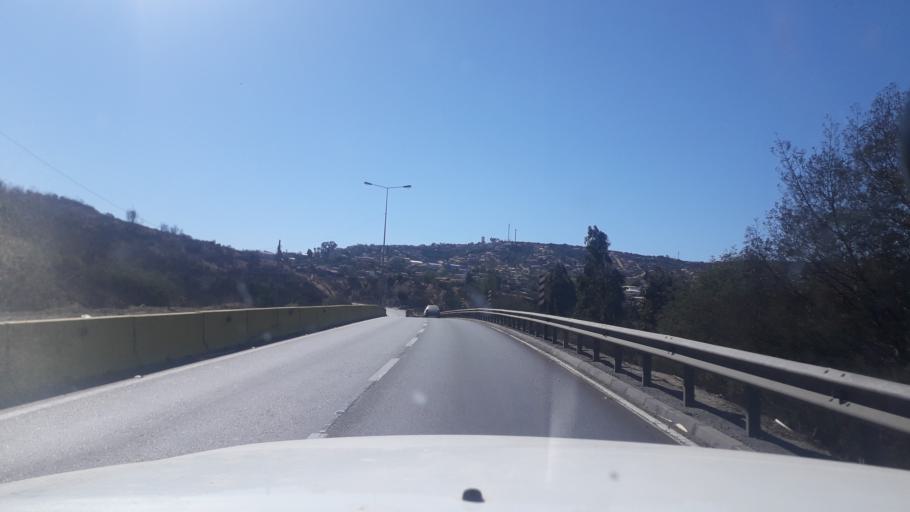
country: CL
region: Valparaiso
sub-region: Provincia de Valparaiso
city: Vina del Mar
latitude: -33.0294
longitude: -71.4994
